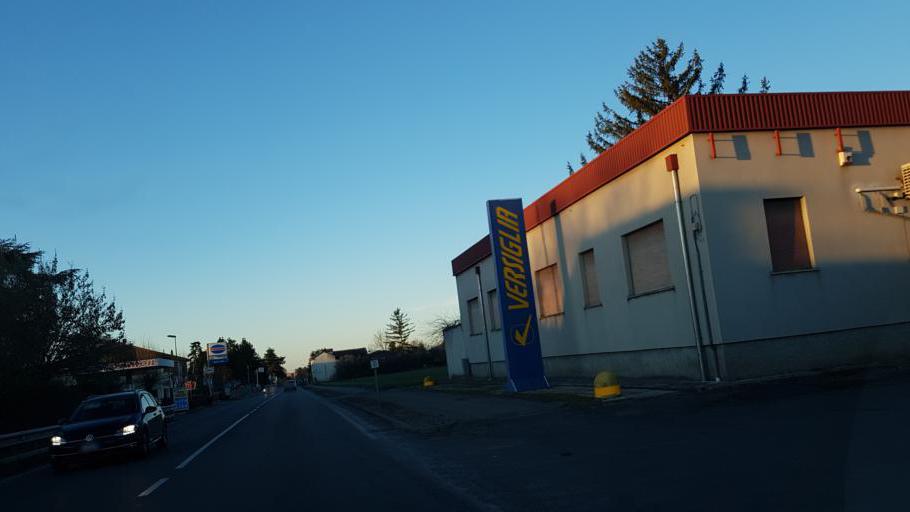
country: IT
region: Piedmont
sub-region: Provincia di Alessandria
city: Tortona
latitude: 44.8728
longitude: 8.8571
